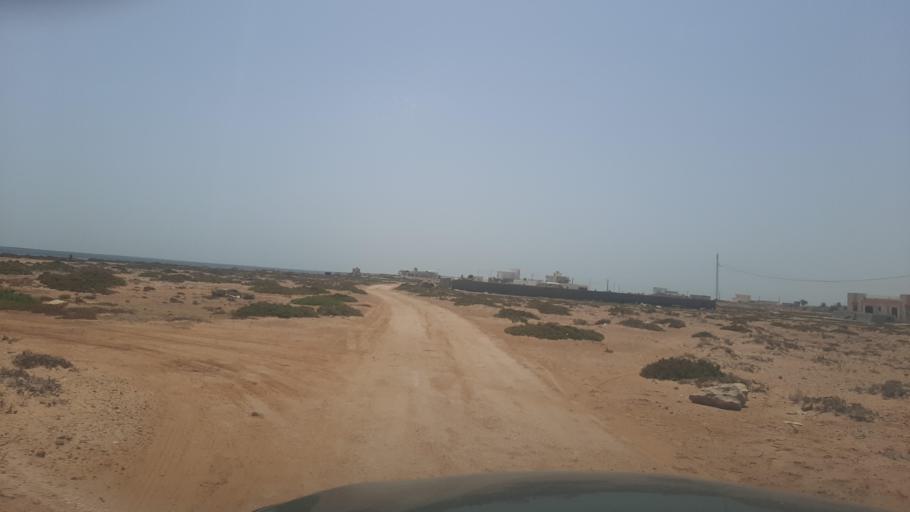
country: TN
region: Al Mahdiyah
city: Mellouleche
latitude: 34.8258
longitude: 11.2583
